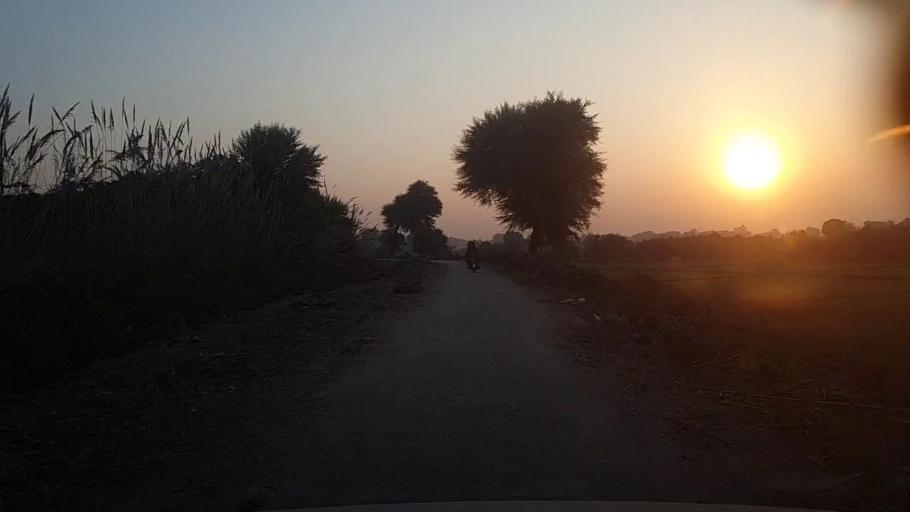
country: PK
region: Sindh
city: Karaundi
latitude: 26.8339
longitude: 68.3671
